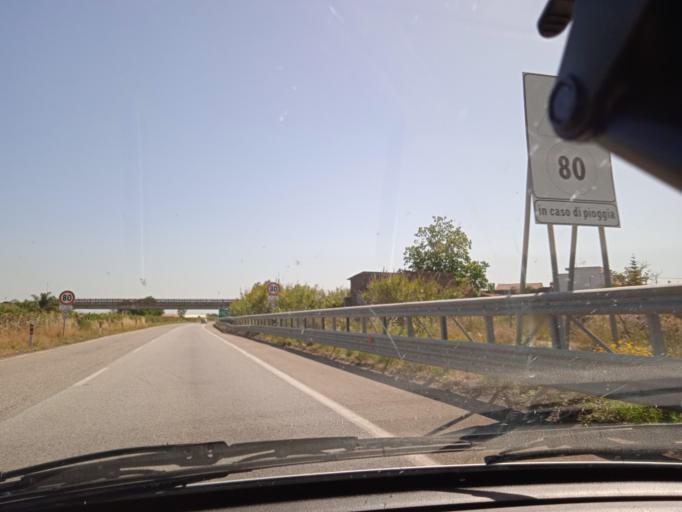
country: IT
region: Sicily
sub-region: Messina
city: Meri
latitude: 38.1780
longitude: 15.2451
